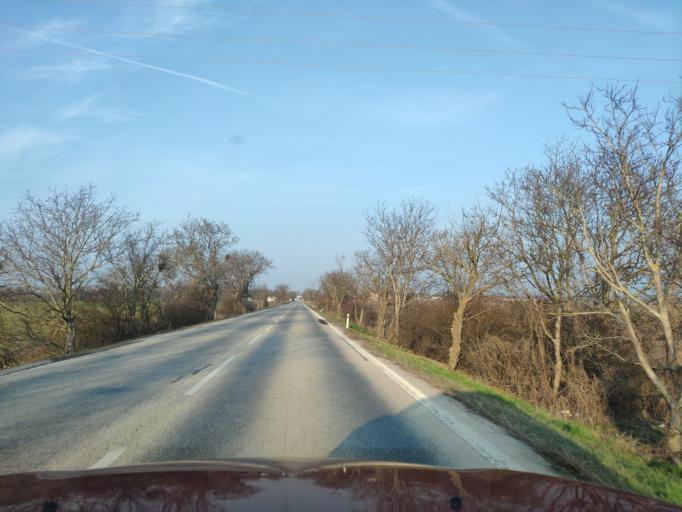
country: SK
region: Trnavsky
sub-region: Okres Trnava
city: Trnava
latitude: 48.3051
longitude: 17.4887
